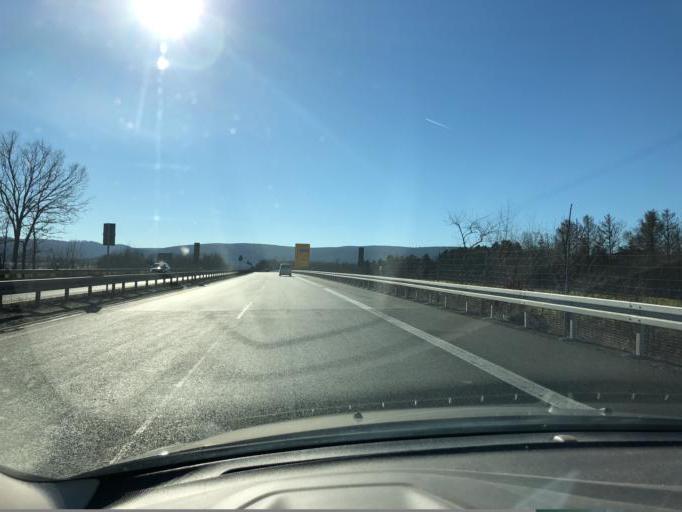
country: DE
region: Lower Saxony
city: Vienenburg
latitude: 51.9210
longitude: 10.5567
